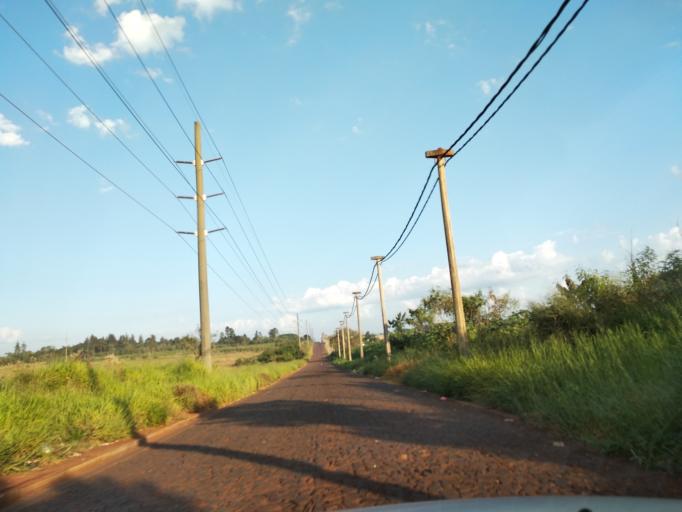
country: AR
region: Misiones
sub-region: Departamento de Capital
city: Posadas
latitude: -27.4428
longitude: -55.9369
